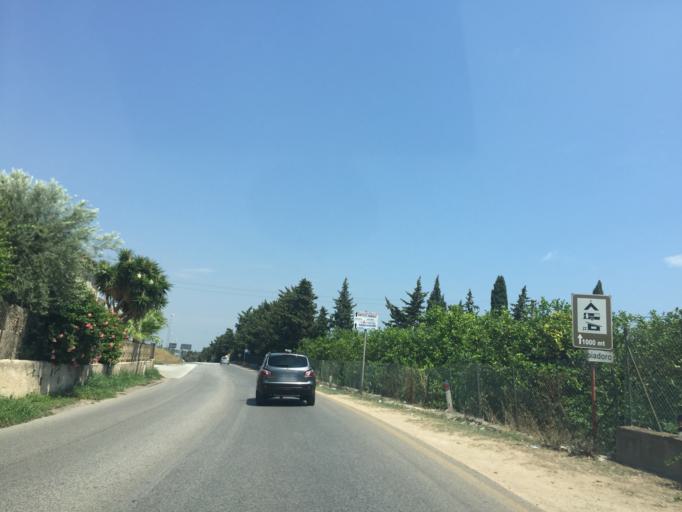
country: IT
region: Sicily
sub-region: Provincia di Siracusa
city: Avola
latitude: 36.9284
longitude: 15.1642
